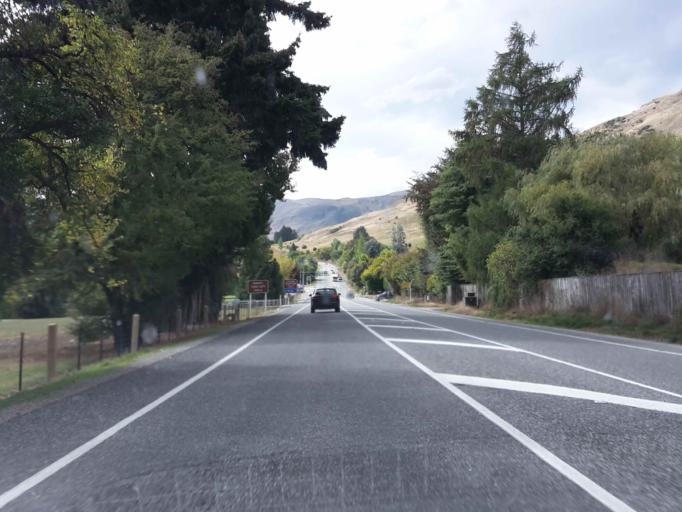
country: NZ
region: Otago
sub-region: Queenstown-Lakes District
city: Arrowtown
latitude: -44.9896
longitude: 168.8113
